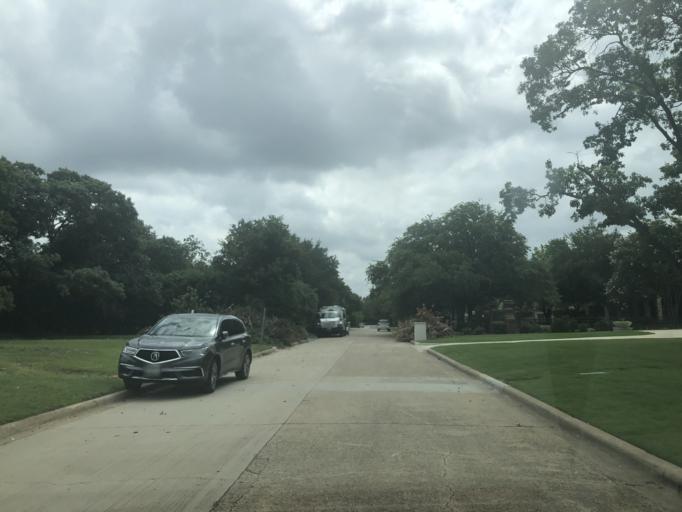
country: US
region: Texas
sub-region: Dallas County
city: University Park
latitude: 32.8897
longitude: -96.8310
